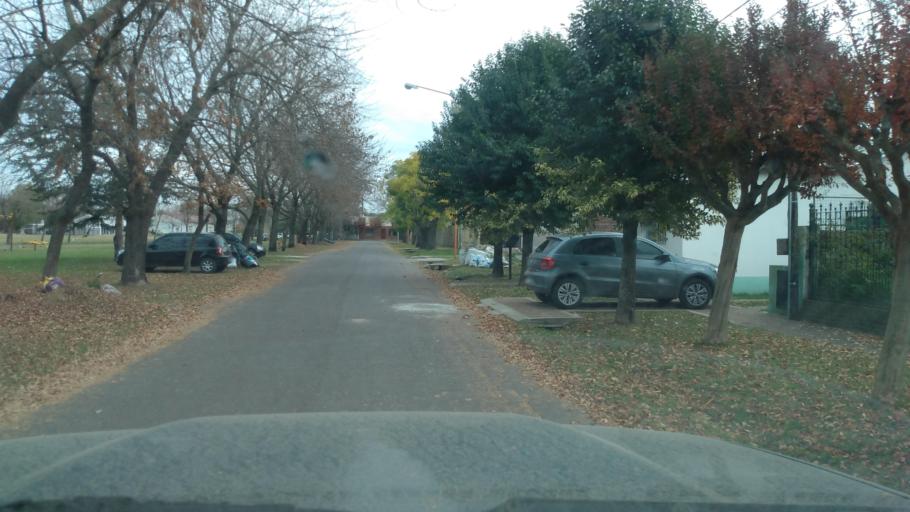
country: AR
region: Buenos Aires
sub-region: Partido de Lujan
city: Lujan
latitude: -34.5988
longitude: -59.1716
